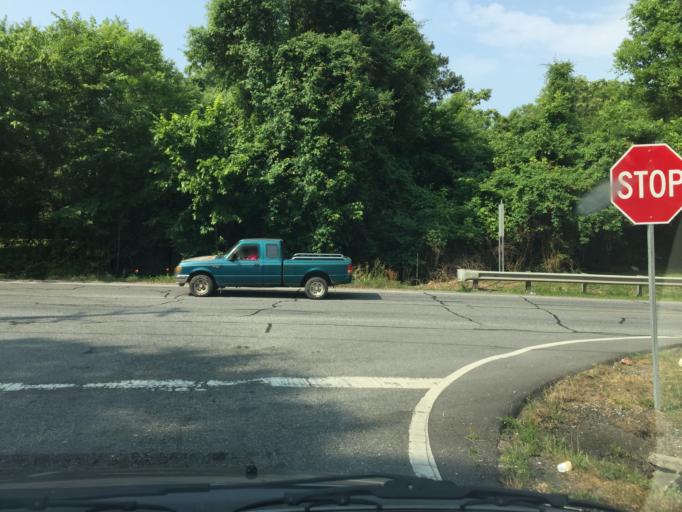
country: US
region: Georgia
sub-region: Catoosa County
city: Ringgold
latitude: 34.9146
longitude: -85.1066
